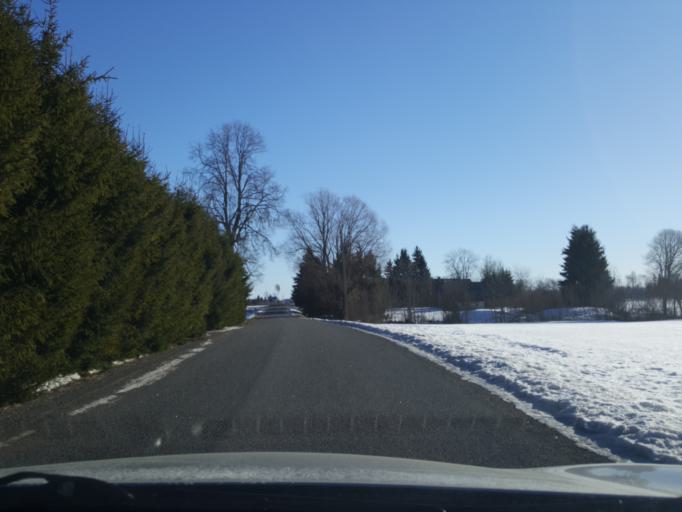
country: EE
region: Viljandimaa
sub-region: Viljandi linn
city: Viljandi
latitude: 58.4608
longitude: 25.5892
